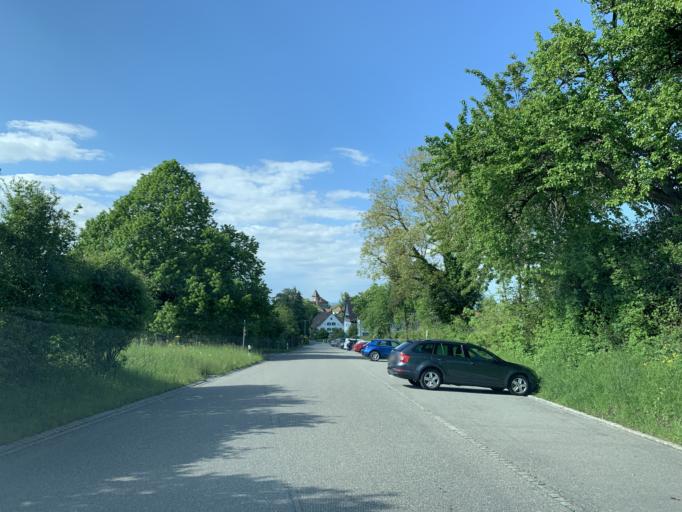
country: CH
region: Zurich
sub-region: Bezirk Winterthur
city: Kollbrunn / Kollbrunn (Dorfkern)
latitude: 47.4521
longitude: 8.7433
